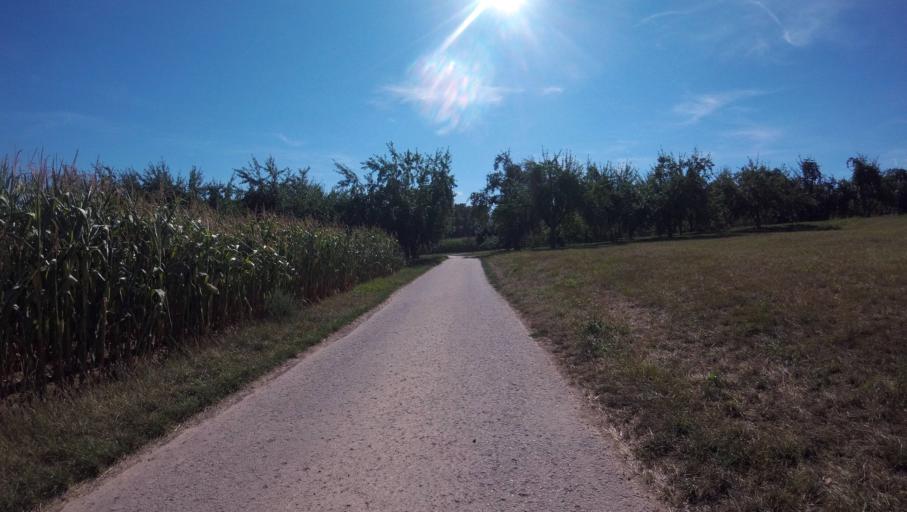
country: DE
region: Baden-Wuerttemberg
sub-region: Regierungsbezirk Stuttgart
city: Mittelschontal
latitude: 48.9401
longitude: 9.3844
